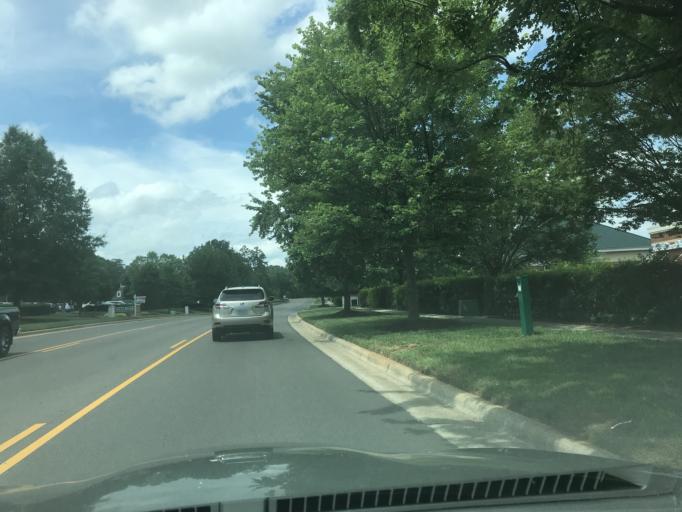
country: US
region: North Carolina
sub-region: Wake County
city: Wake Forest
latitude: 35.9069
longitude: -78.5908
